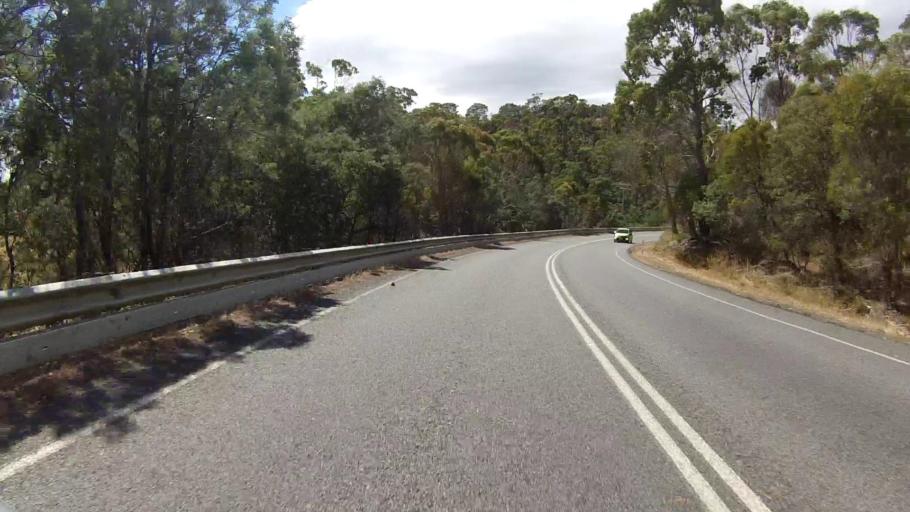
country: AU
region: Tasmania
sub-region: Sorell
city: Sorell
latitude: -42.6069
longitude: 147.6713
